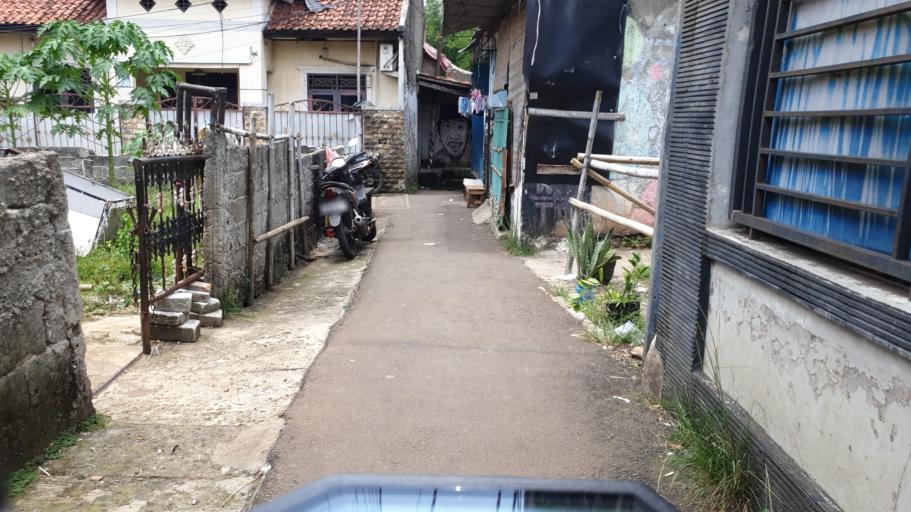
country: ID
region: West Java
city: Depok
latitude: -6.3297
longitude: 106.8322
